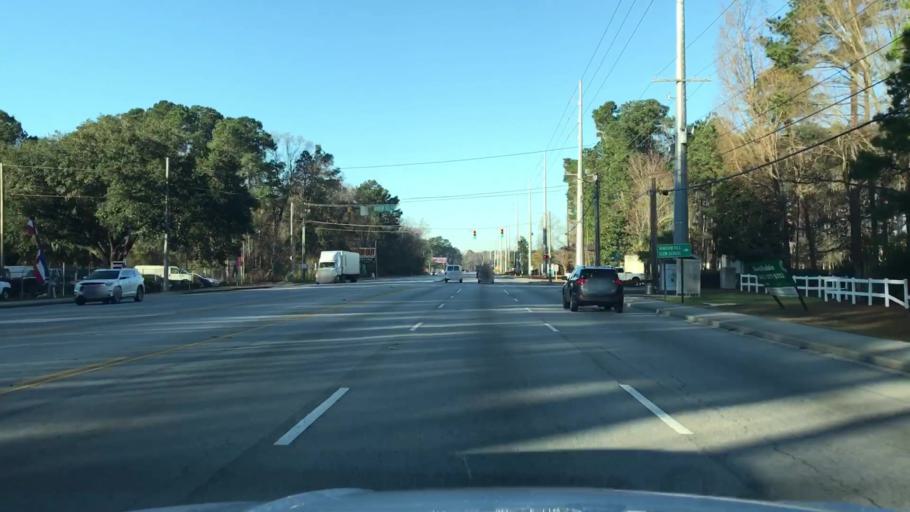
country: US
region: South Carolina
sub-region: Berkeley County
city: Ladson
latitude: 32.9240
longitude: -80.0886
